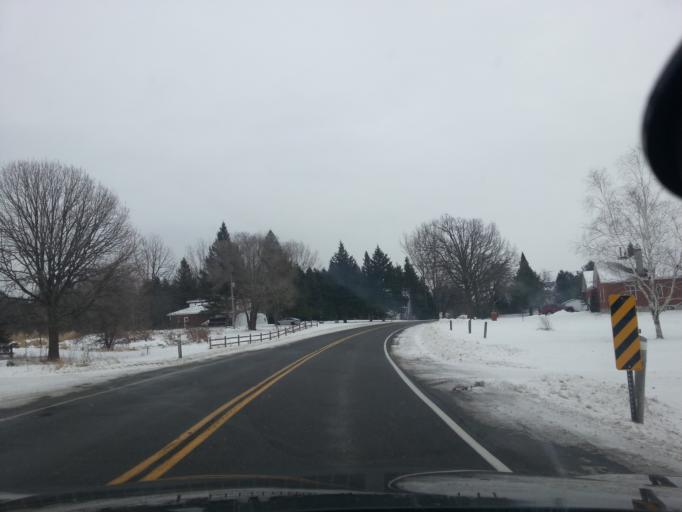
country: CA
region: Ontario
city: Bells Corners
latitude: 45.3574
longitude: -76.0523
